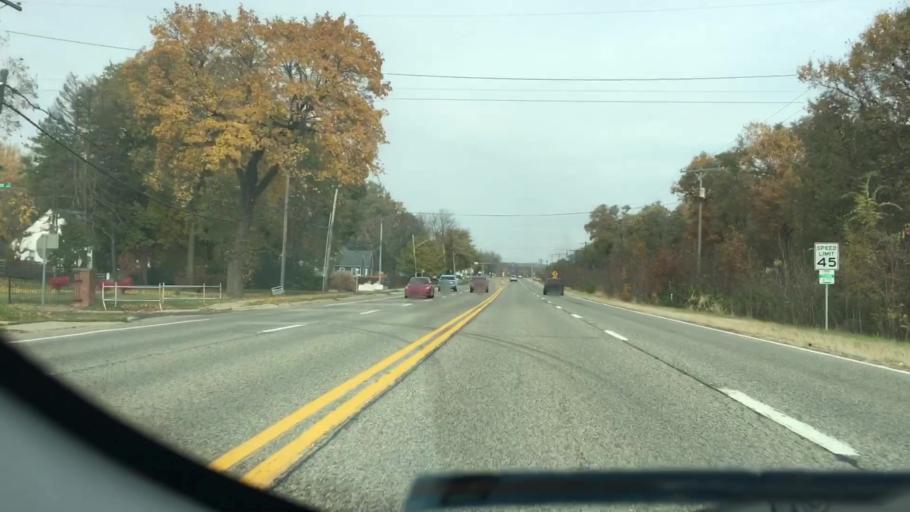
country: US
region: Illinois
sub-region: Peoria County
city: Peoria Heights
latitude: 40.7552
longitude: -89.5629
